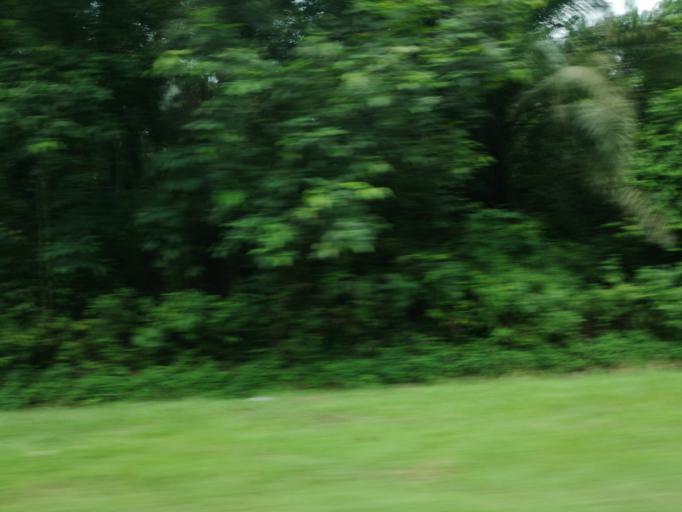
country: MY
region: Penang
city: Tasek Glugor
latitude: 5.4933
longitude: 100.6065
